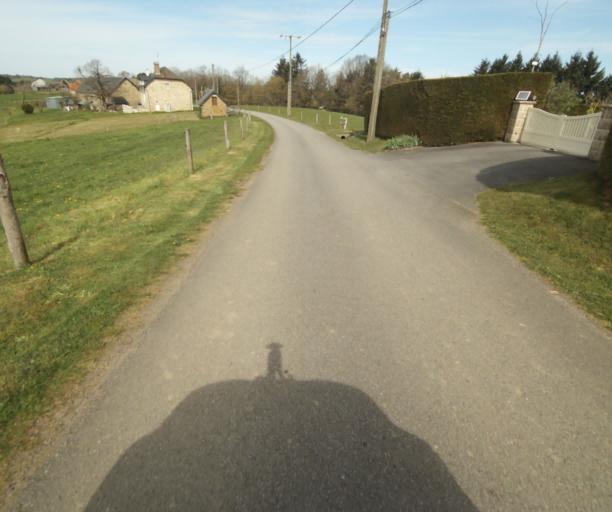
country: FR
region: Limousin
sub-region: Departement de la Correze
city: Correze
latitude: 45.3924
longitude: 1.8126
